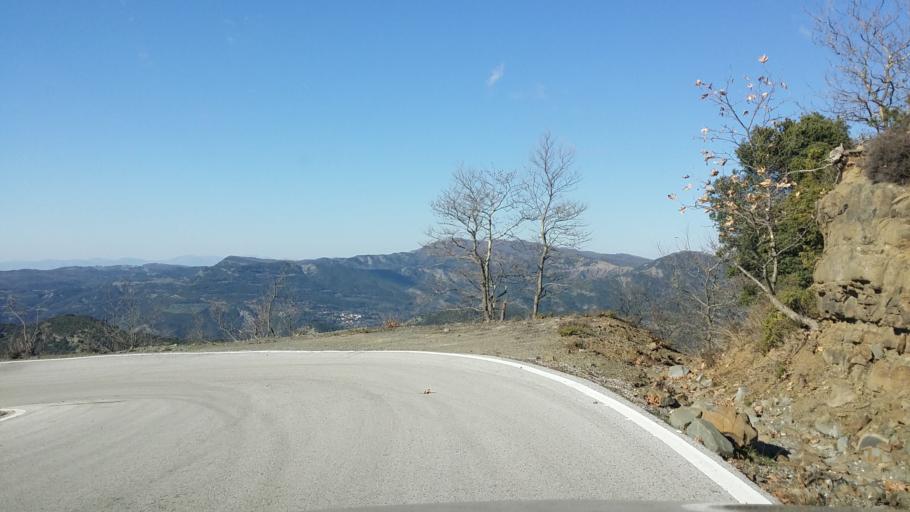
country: GR
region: West Greece
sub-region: Nomos Aitolias kai Akarnanias
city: Krikellos
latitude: 38.9775
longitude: 21.2728
